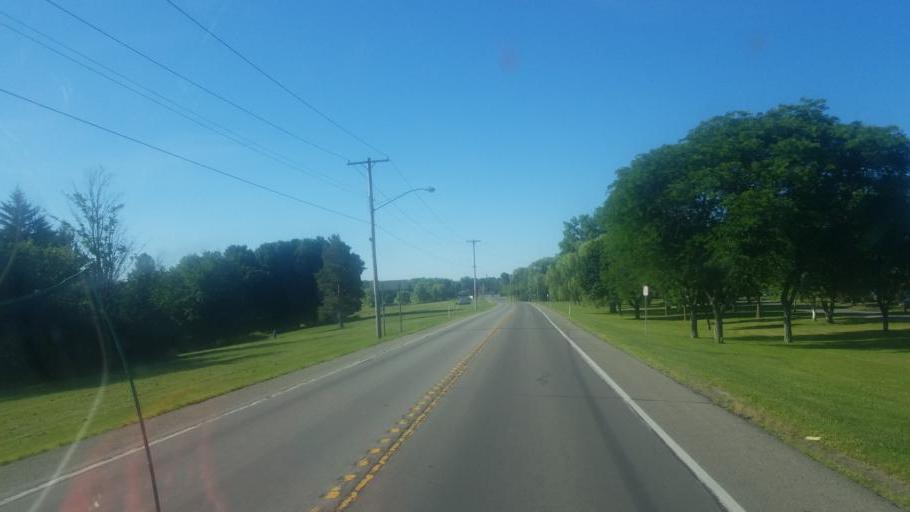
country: US
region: New York
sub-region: Wayne County
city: Newark
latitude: 43.0271
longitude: -77.0961
